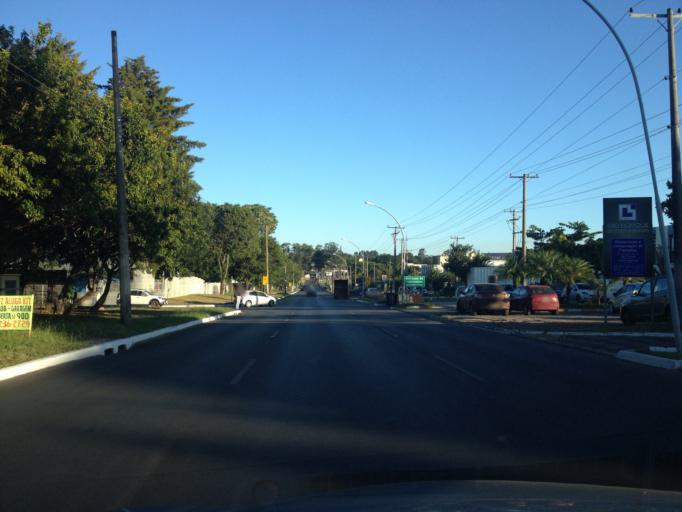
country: BR
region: Federal District
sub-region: Brasilia
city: Brasilia
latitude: -15.7533
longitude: -47.8989
